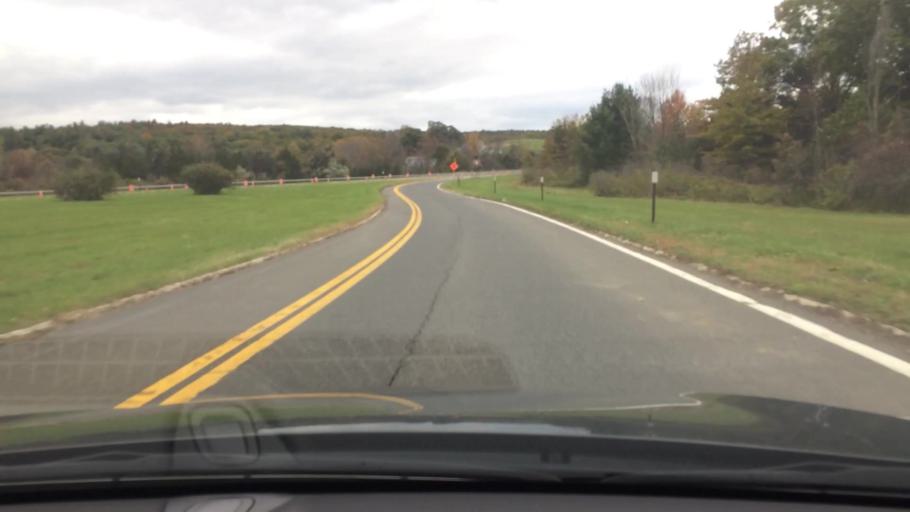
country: US
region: New York
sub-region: Columbia County
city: Philmont
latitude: 42.1164
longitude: -73.7159
